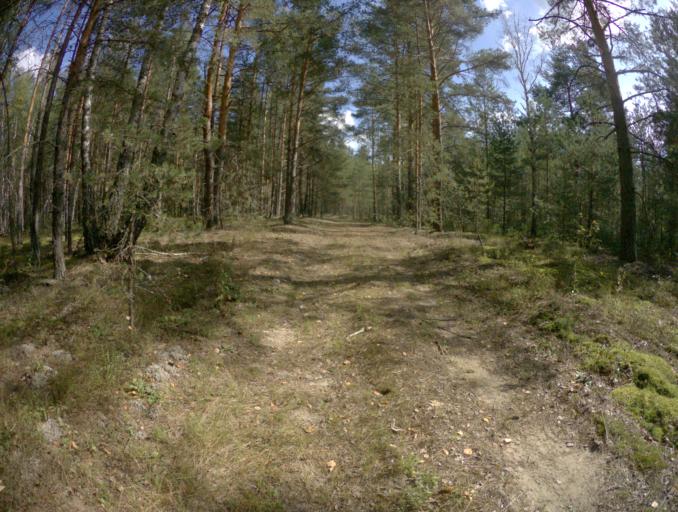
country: RU
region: Vladimir
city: Pokrov
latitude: 55.8449
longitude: 39.2115
